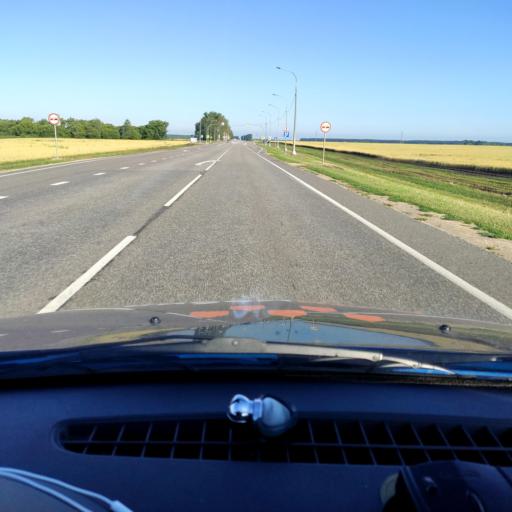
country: RU
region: Orjol
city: Pokrovskoye
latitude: 52.6269
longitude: 36.7121
